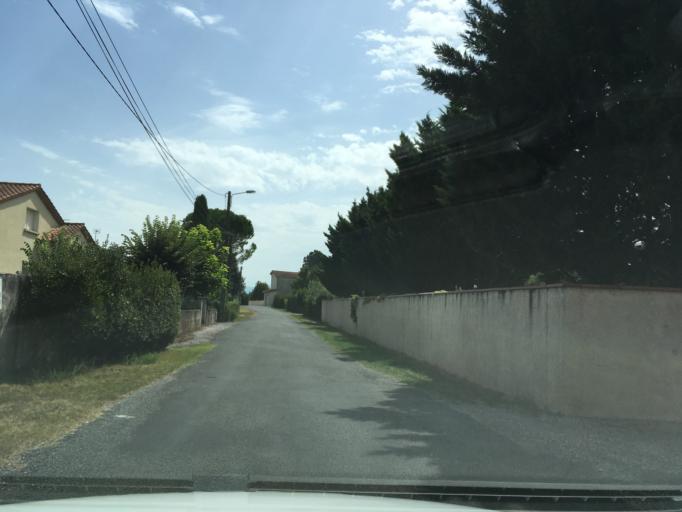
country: FR
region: Midi-Pyrenees
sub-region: Departement du Tarn
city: Castres
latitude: 43.6135
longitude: 2.2192
